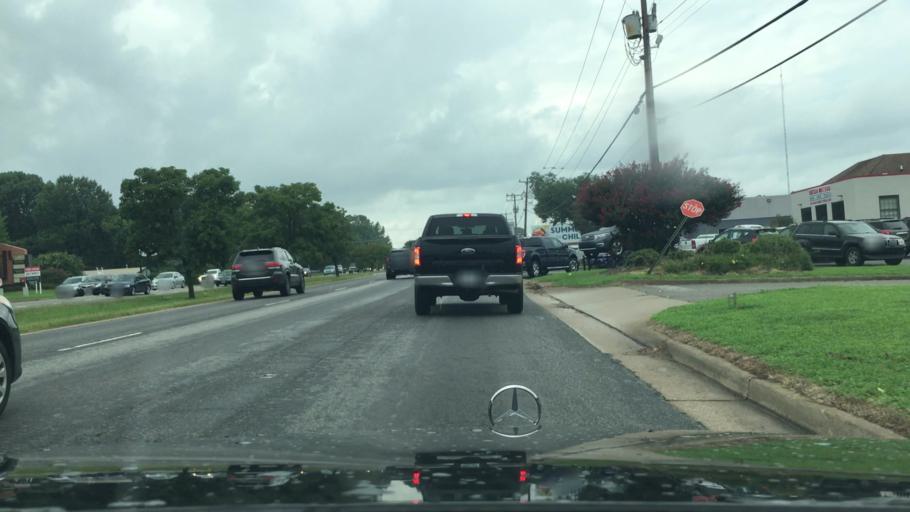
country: US
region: Virginia
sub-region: Chesterfield County
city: Bon Air
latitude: 37.4989
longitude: -77.5695
